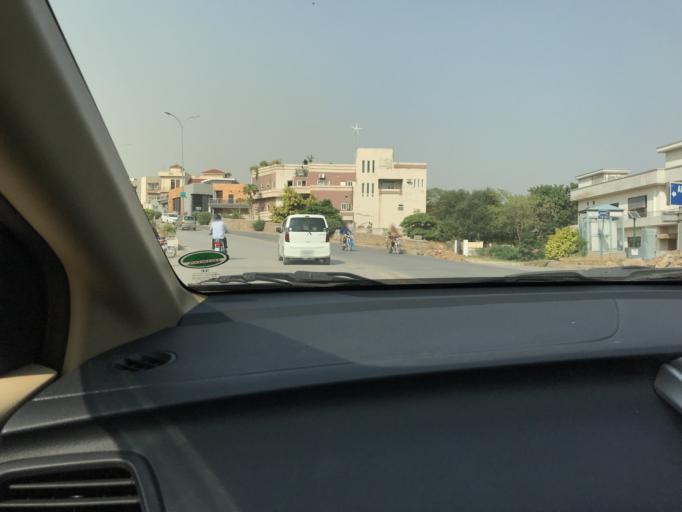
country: PK
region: Punjab
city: Rawalpindi
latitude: 33.5279
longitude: 73.1056
